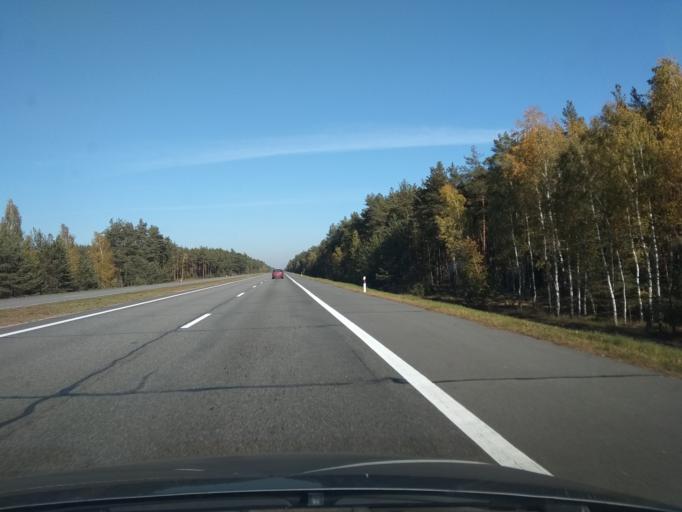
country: BY
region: Grodnenskaya
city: Zhyrovichy
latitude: 52.9309
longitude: 25.6971
